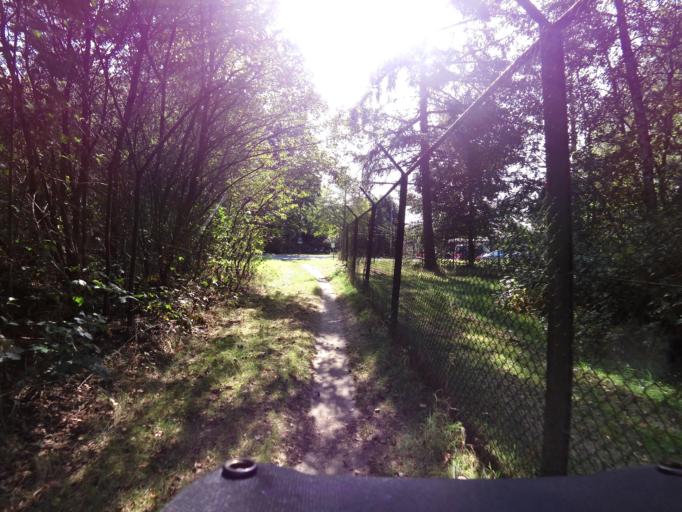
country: NL
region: Gelderland
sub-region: Gemeente Apeldoorn
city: Uddel
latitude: 52.2249
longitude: 5.7750
